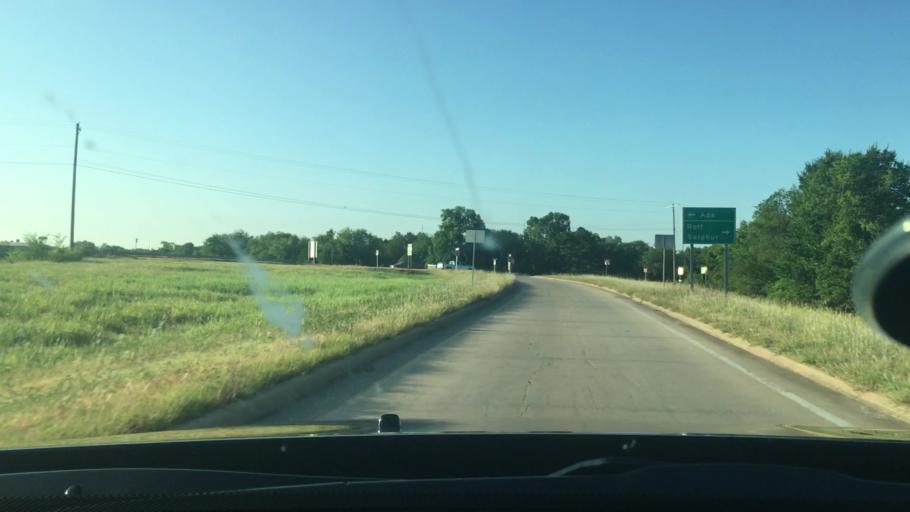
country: US
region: Oklahoma
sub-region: Pontotoc County
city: Ada
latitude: 34.7642
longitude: -96.7032
